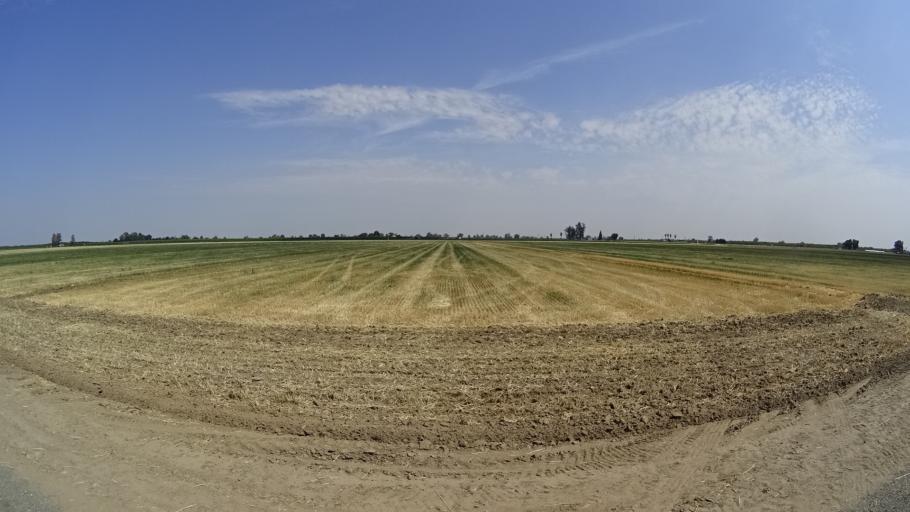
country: US
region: California
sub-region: Fresno County
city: Riverdale
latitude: 36.3948
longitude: -119.7899
